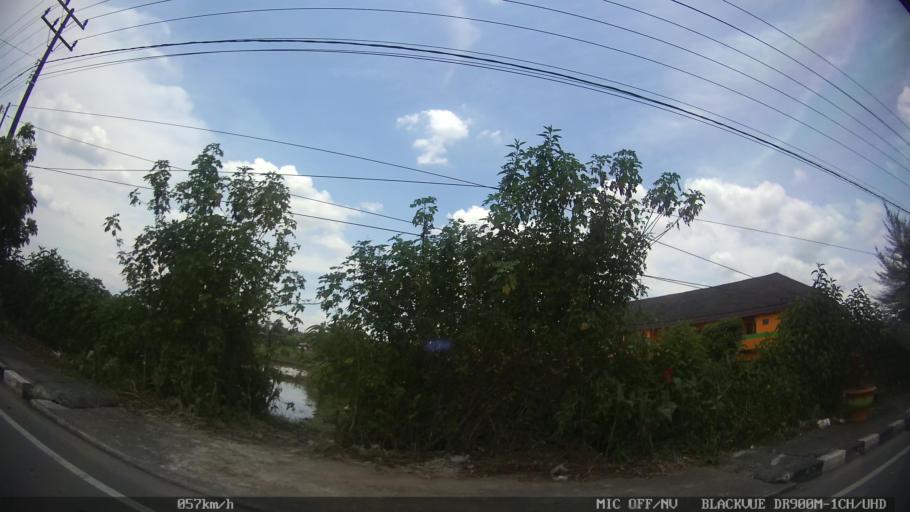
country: ID
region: North Sumatra
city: Binjai
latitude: 3.6043
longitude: 98.5313
